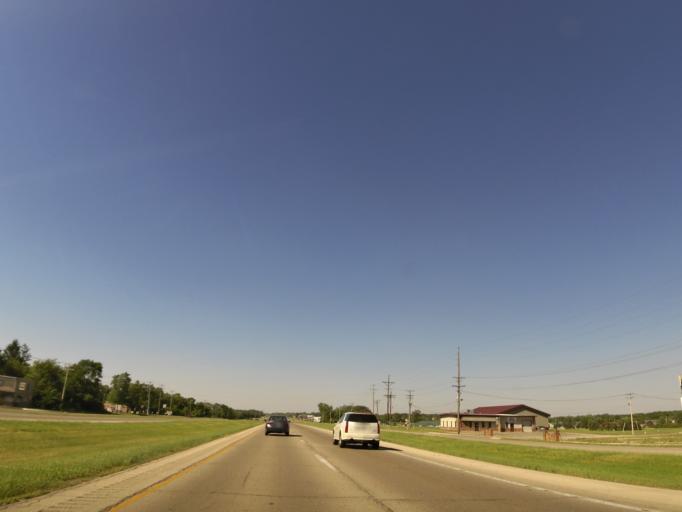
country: US
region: Illinois
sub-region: Winnebago County
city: Roscoe
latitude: 42.3851
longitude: -89.0196
